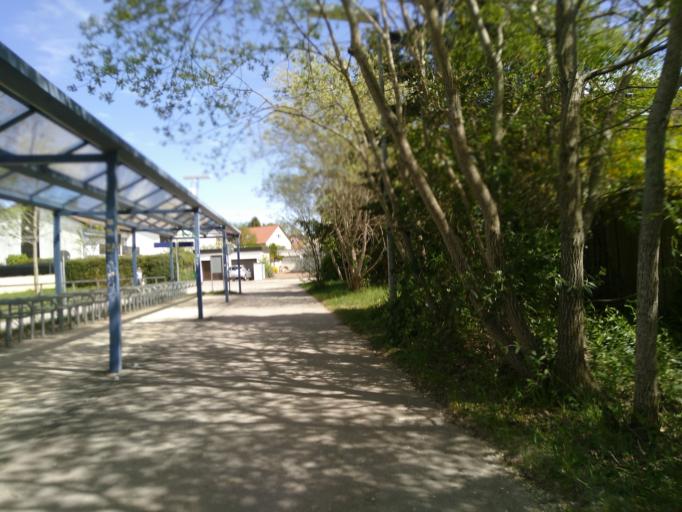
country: DE
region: Bavaria
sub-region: Upper Bavaria
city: Unterhaching
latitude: 48.0938
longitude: 11.6059
